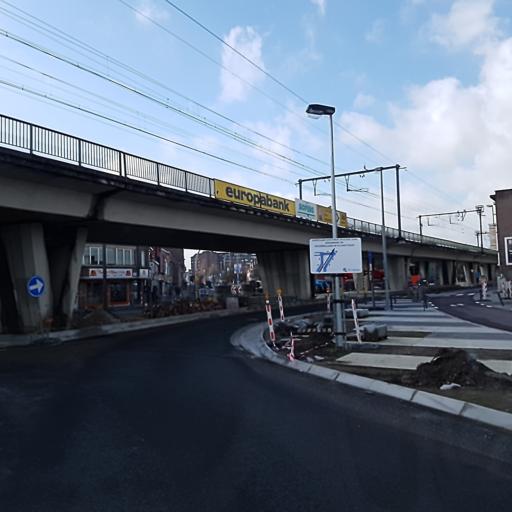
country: BE
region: Flanders
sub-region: Provincie Oost-Vlaanderen
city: Sint-Niklaas
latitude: 51.1700
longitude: 4.1394
